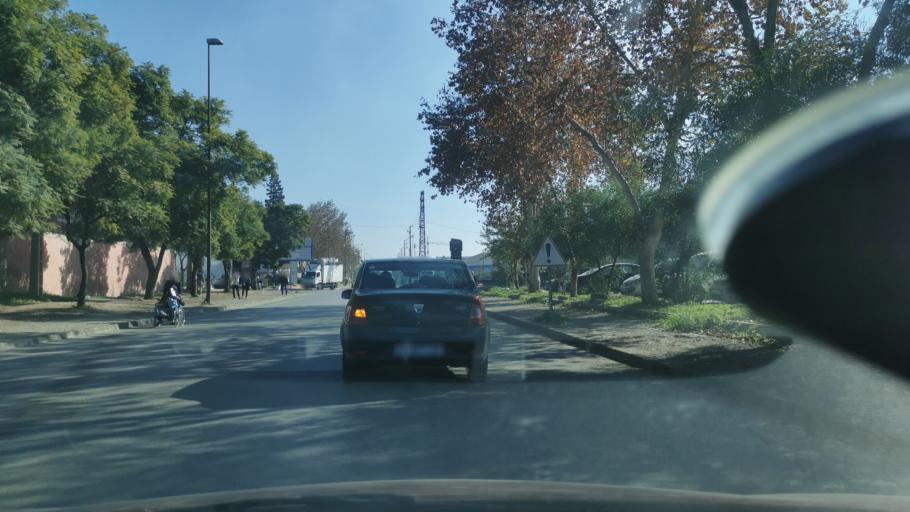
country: MA
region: Fes-Boulemane
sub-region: Fes
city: Fes
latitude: 34.0307
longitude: -4.9841
